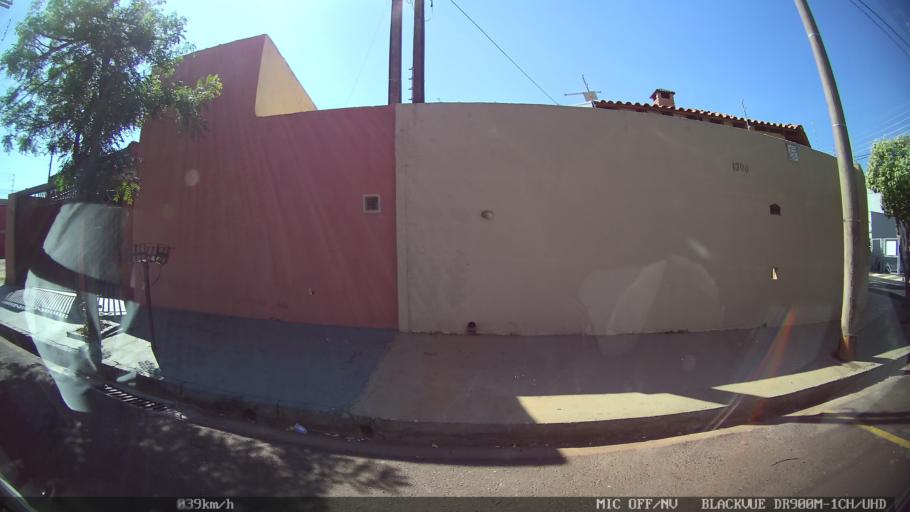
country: BR
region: Sao Paulo
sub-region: Sao Jose Do Rio Preto
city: Sao Jose do Rio Preto
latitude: -20.7835
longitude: -49.4148
